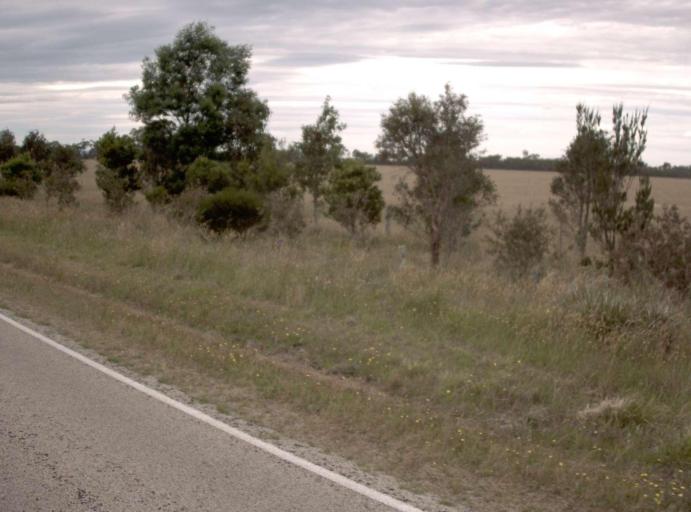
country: AU
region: Victoria
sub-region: East Gippsland
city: Bairnsdale
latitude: -37.9044
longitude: 147.5519
